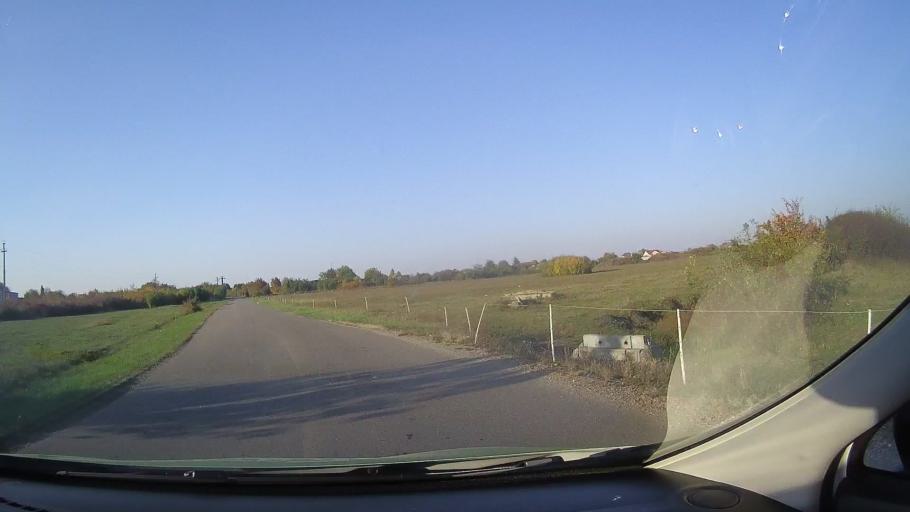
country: RO
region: Bihor
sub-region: Comuna Bors
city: Bors
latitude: 47.1114
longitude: 21.8242
